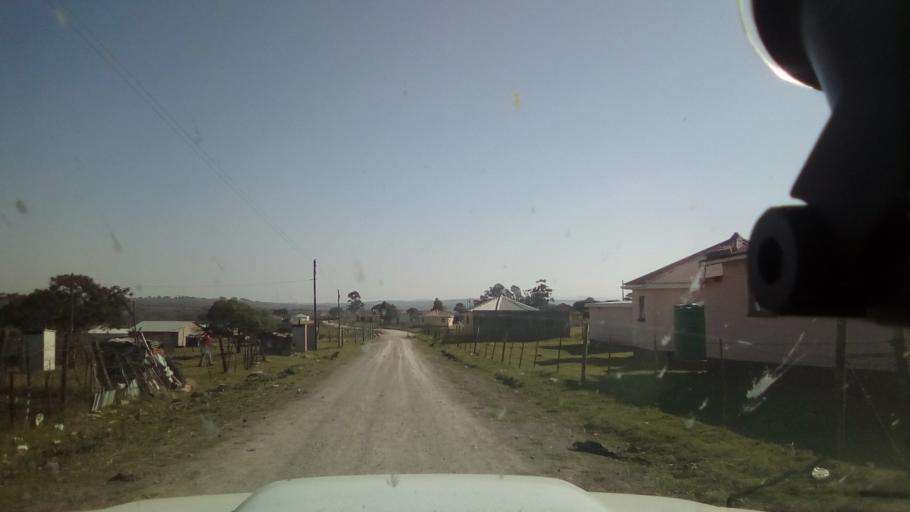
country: ZA
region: Eastern Cape
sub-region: Buffalo City Metropolitan Municipality
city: Bhisho
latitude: -32.9410
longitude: 27.3300
